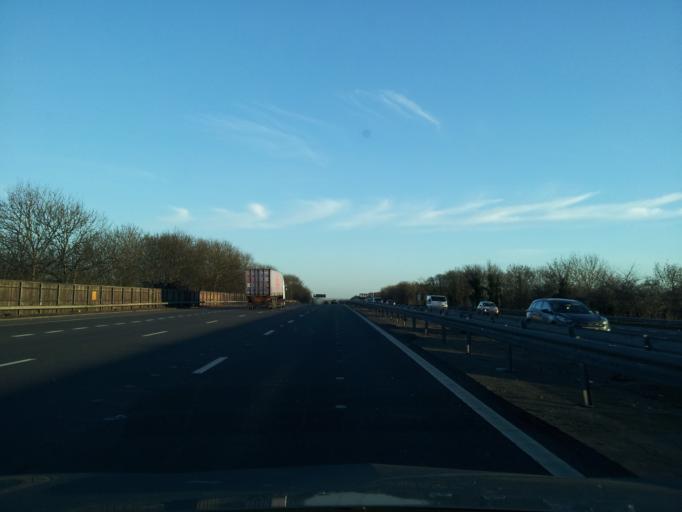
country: GB
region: England
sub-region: Milton Keynes
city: Newport Pagnell
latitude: 52.0820
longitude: -0.7462
